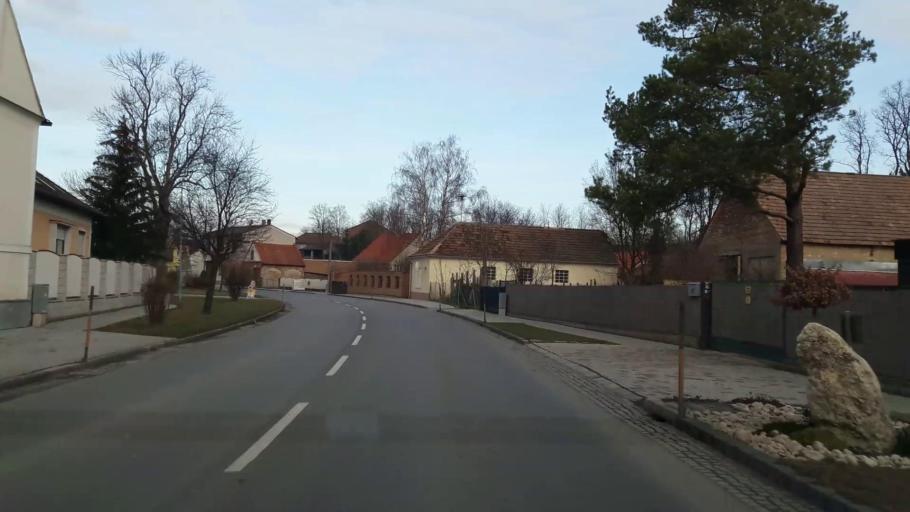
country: AT
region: Lower Austria
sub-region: Politischer Bezirk Mistelbach
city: Staatz
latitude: 48.6617
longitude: 16.4957
